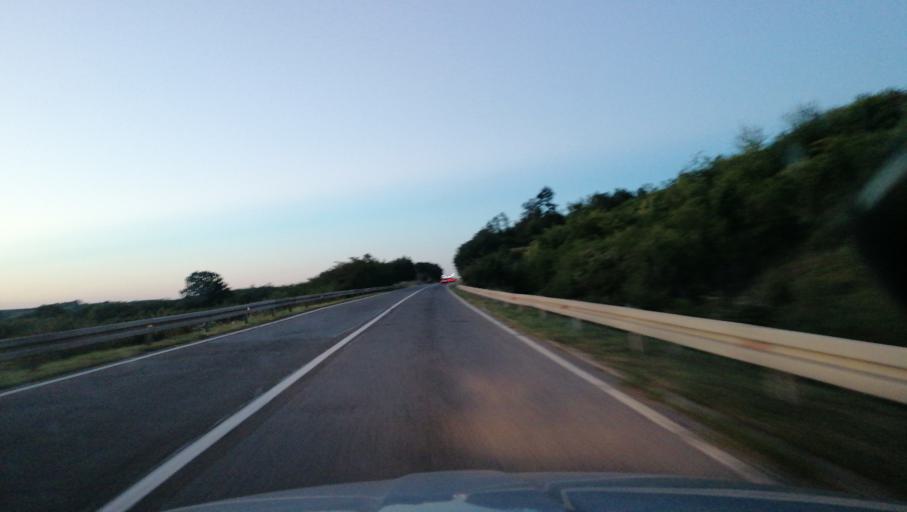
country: RS
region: Central Serbia
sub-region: Belgrade
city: Sopot
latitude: 44.5320
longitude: 20.6563
